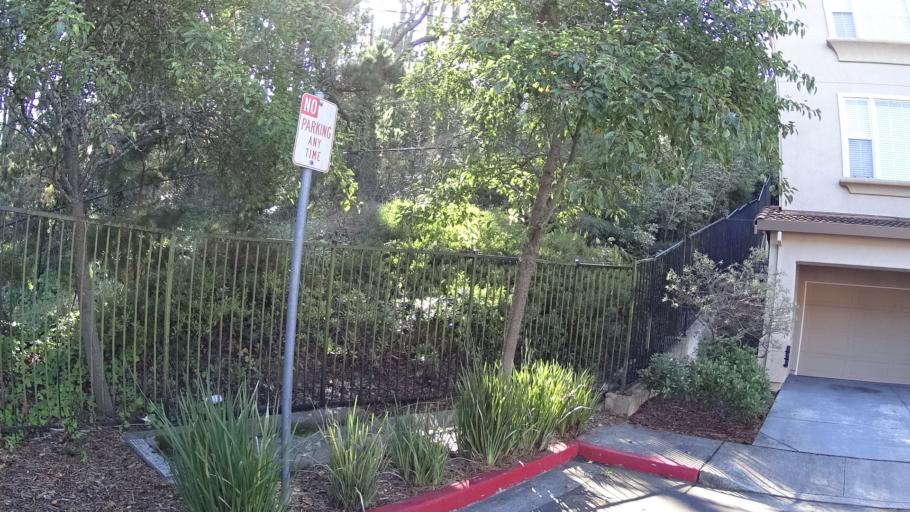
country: US
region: California
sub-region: San Mateo County
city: Pacifica
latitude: 37.6397
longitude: -122.4619
